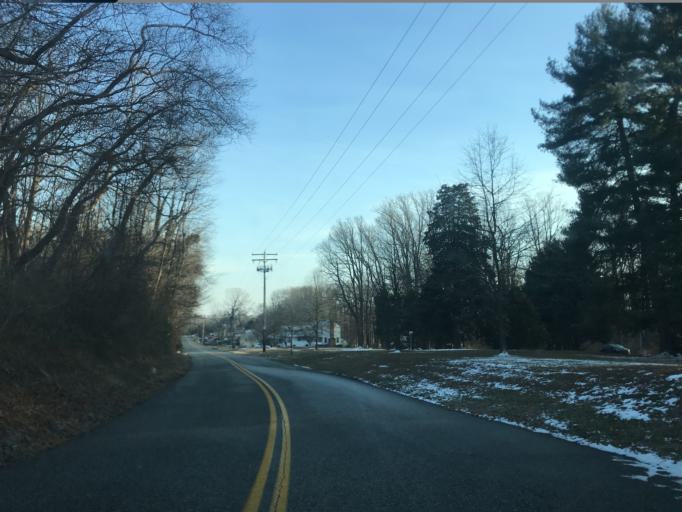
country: US
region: Maryland
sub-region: Harford County
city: Edgewood
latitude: 39.4056
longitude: -76.3310
